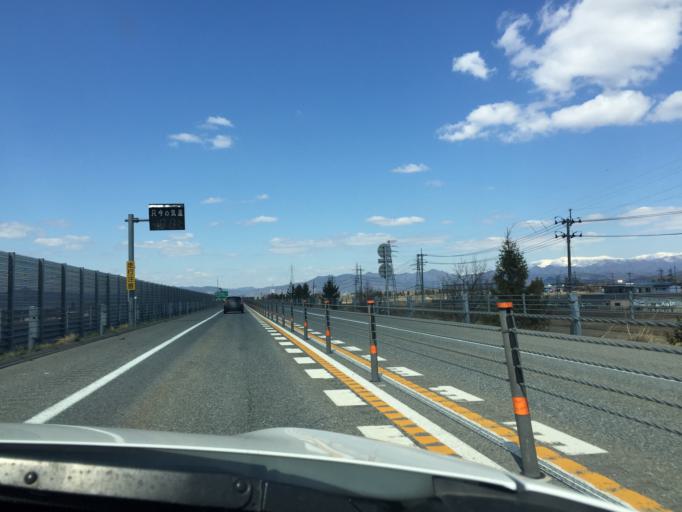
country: JP
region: Yamagata
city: Yonezawa
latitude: 37.9631
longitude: 140.1206
